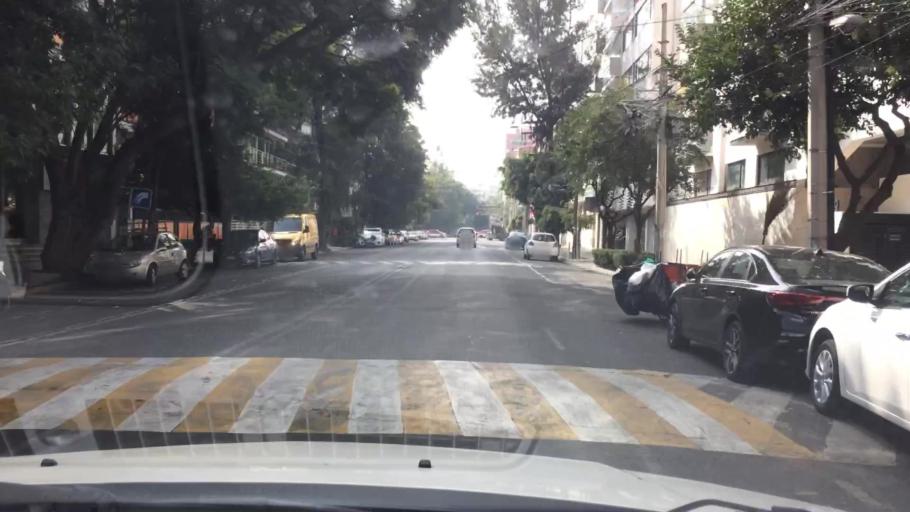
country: MX
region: Mexico City
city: Colonia del Valle
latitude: 19.3873
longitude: -99.1773
